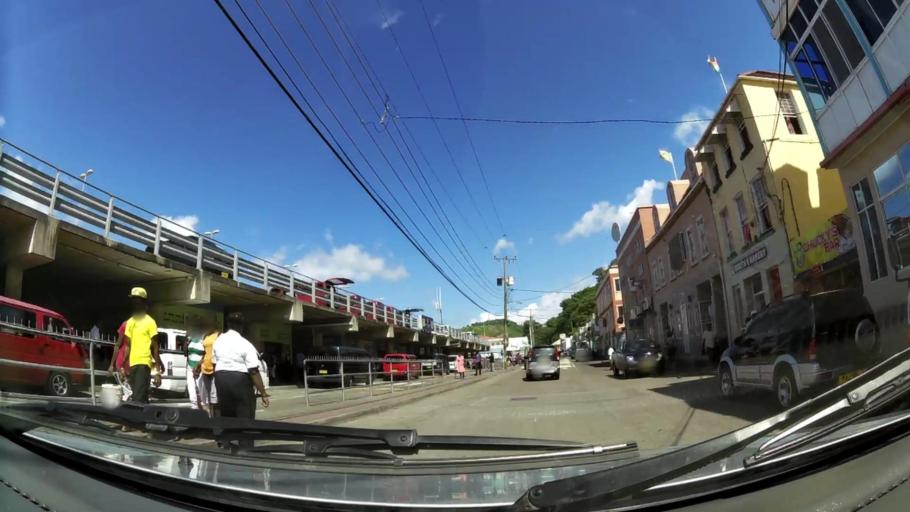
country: GD
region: Saint George
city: Saint George's
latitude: 12.0533
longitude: -61.7548
